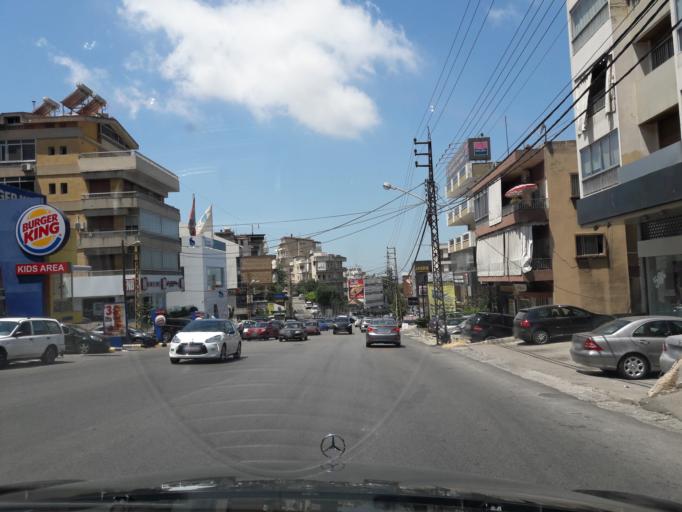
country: LB
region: Mont-Liban
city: Djounie
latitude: 33.9260
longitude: 35.6301
